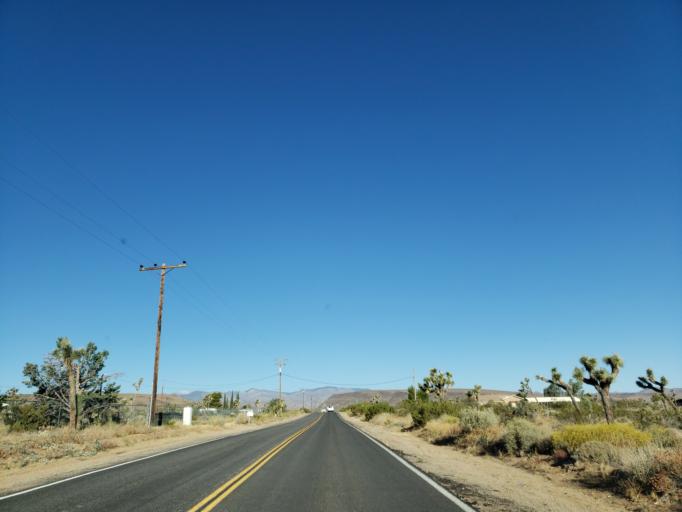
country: US
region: California
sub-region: San Bernardino County
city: Yucca Valley
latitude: 34.1935
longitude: -116.4102
